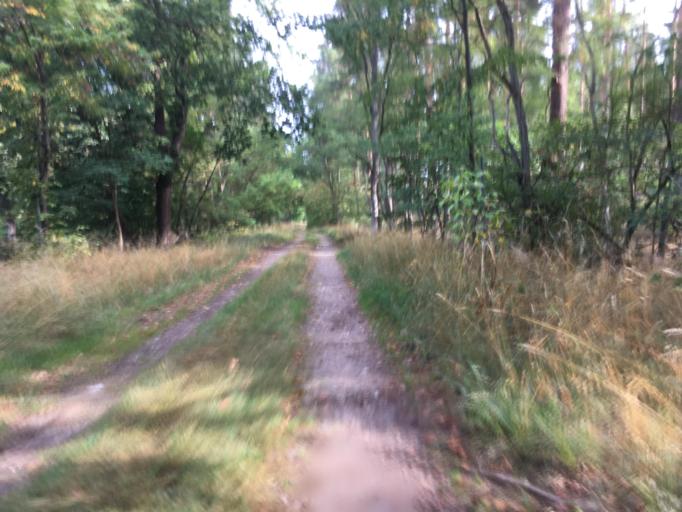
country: DE
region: Brandenburg
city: Marienwerder
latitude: 52.9688
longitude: 13.5306
